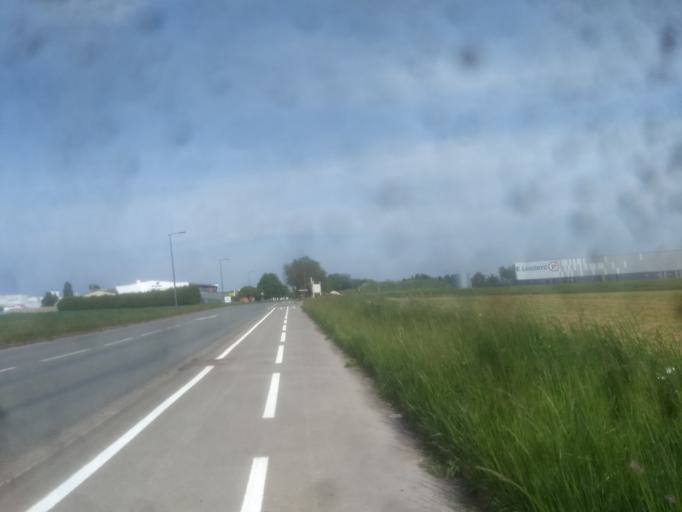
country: FR
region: Nord-Pas-de-Calais
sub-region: Departement du Pas-de-Calais
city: Tilloy-les-Mofflaines
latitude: 50.2827
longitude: 2.8140
